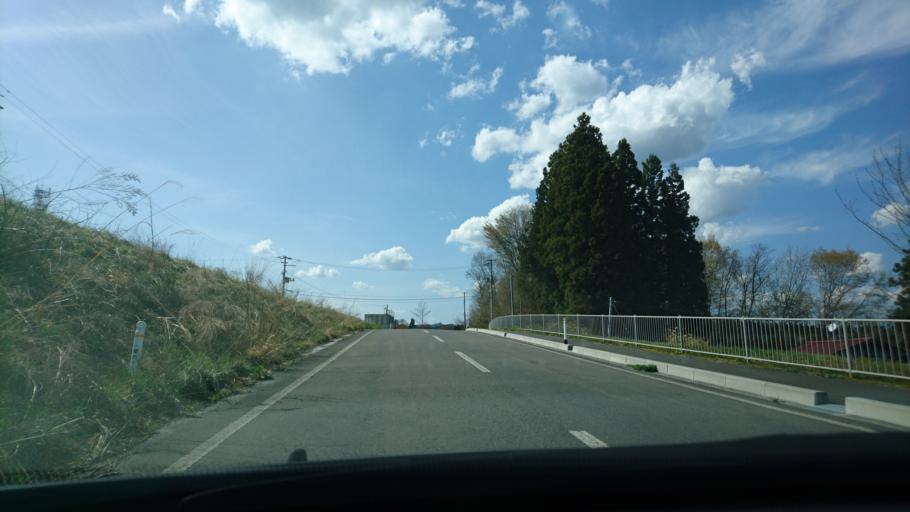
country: JP
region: Iwate
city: Ichinoseki
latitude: 38.9219
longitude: 141.3484
